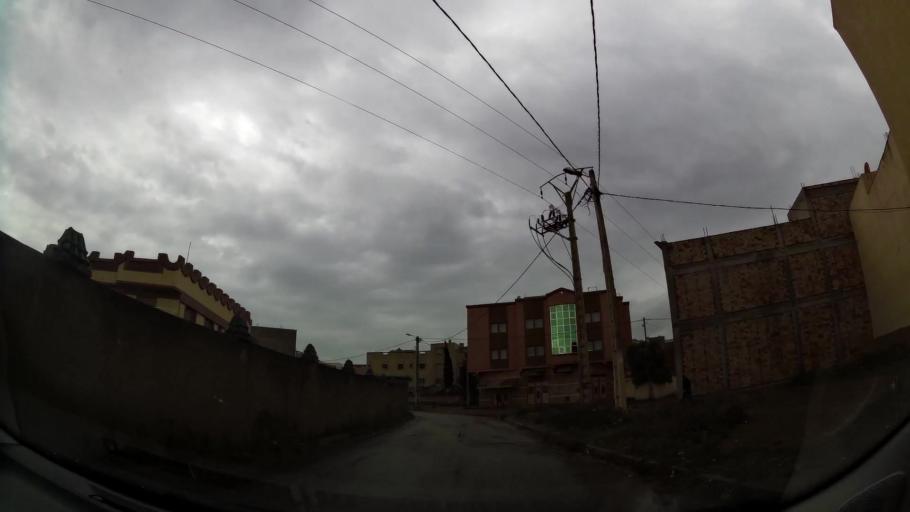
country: MA
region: Oriental
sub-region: Nador
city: Nador
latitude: 35.1504
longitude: -2.9984
